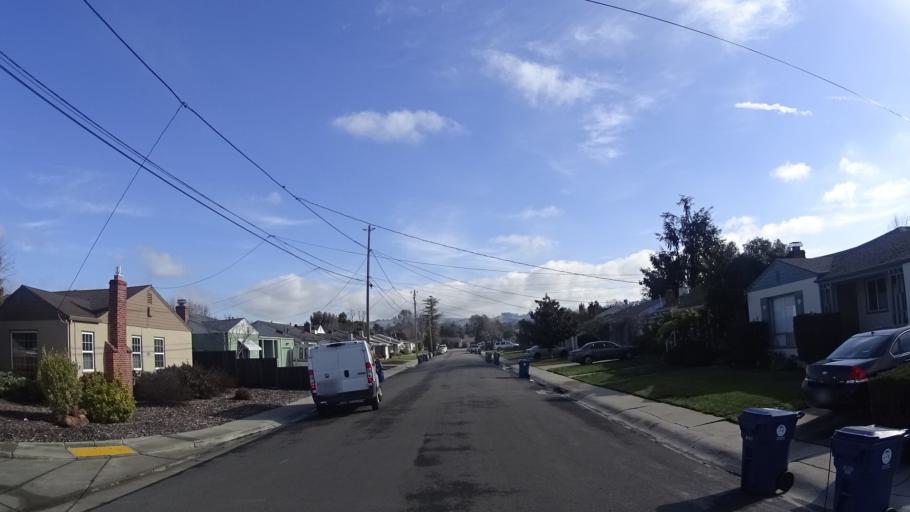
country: US
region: California
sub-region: Alameda County
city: Castro Valley
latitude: 37.6887
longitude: -122.0770
